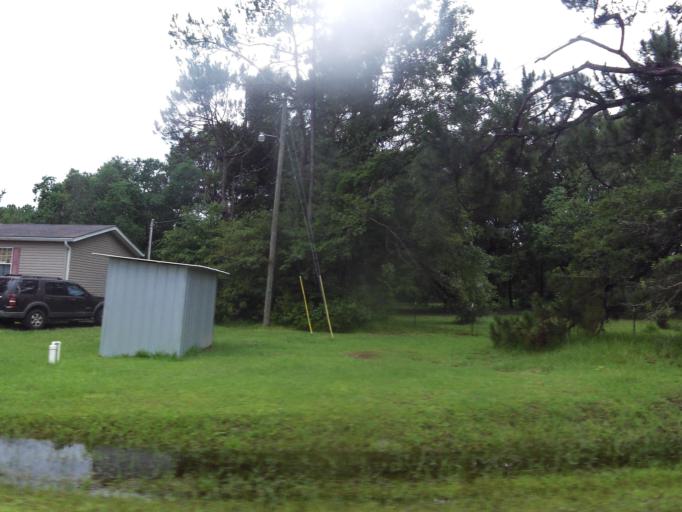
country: US
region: Florida
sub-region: Nassau County
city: Nassau Village-Ratliff
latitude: 30.5086
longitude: -81.8045
